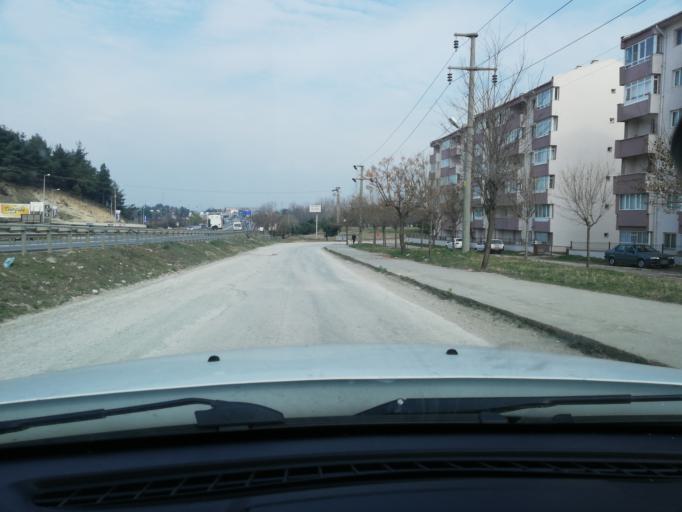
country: TR
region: Edirne
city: Kesan
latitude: 40.8697
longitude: 26.6298
